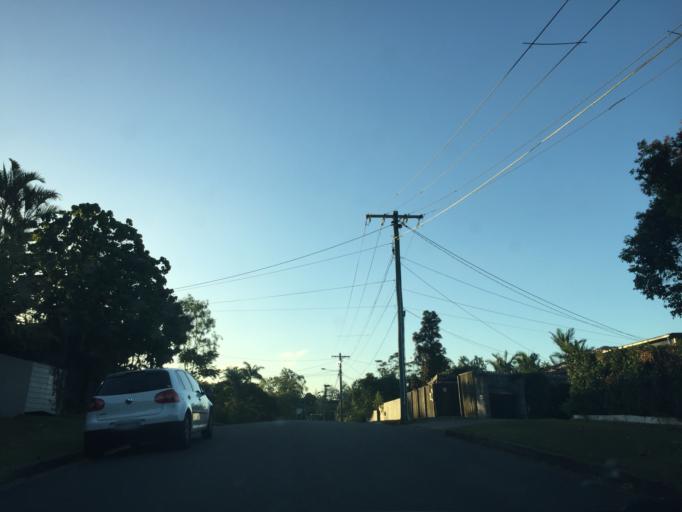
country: AU
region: Queensland
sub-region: Brisbane
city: Taringa
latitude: -27.4539
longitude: 152.9495
